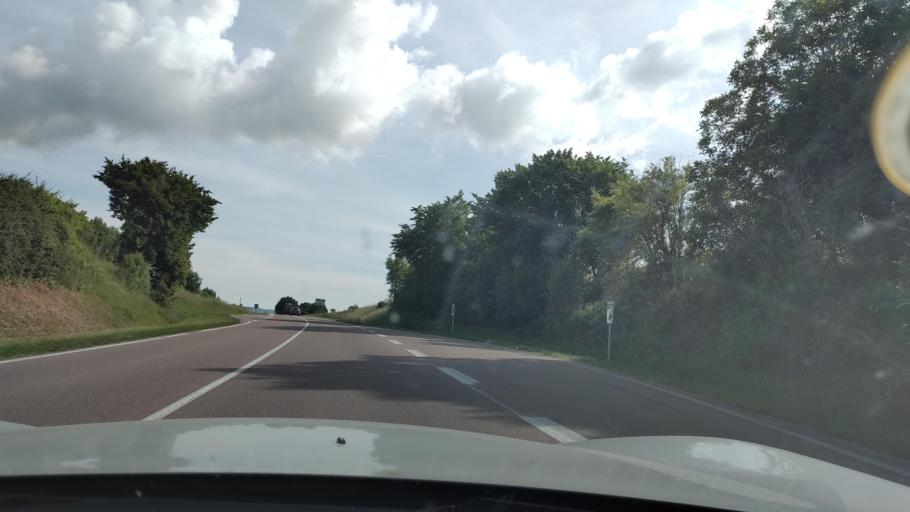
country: FR
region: Champagne-Ardenne
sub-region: Departement de l'Aube
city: Nogent-sur-Seine
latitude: 48.4869
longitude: 3.5184
